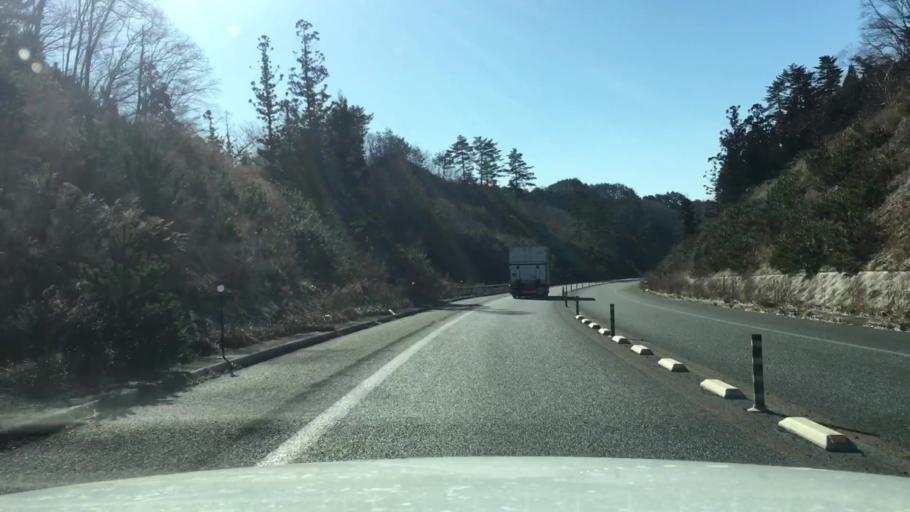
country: JP
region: Iwate
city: Miyako
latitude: 39.6135
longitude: 141.9350
